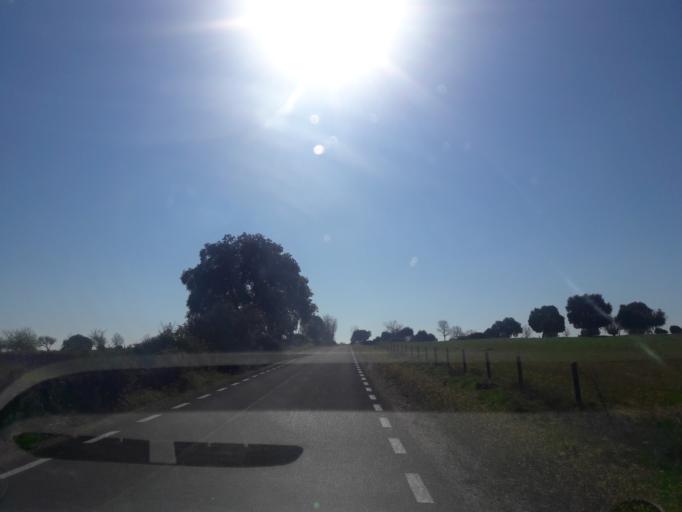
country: ES
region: Castille and Leon
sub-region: Provincia de Salamanca
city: Cabeza del Caballo
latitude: 41.1739
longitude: -6.5107
